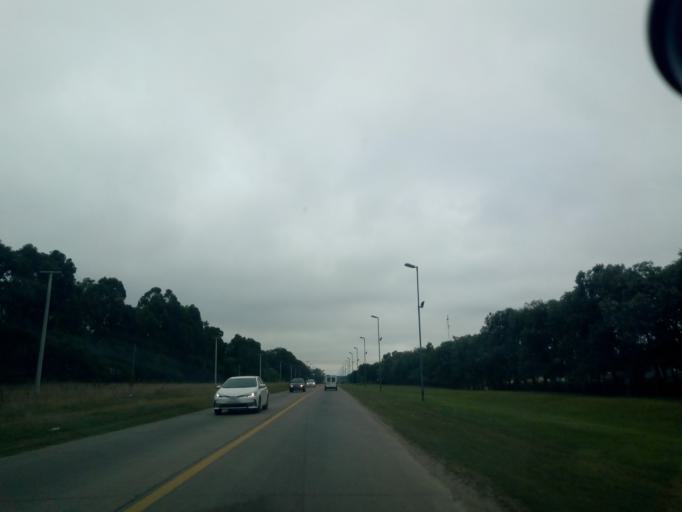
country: AR
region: Buenos Aires
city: Mar del Plata
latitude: -38.0738
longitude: -57.5772
